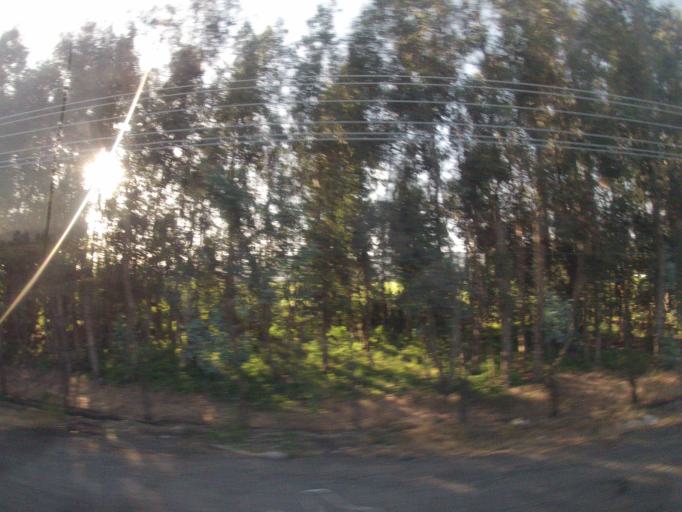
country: CL
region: O'Higgins
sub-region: Provincia de Colchagua
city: Chimbarongo
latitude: -34.7239
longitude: -71.0349
